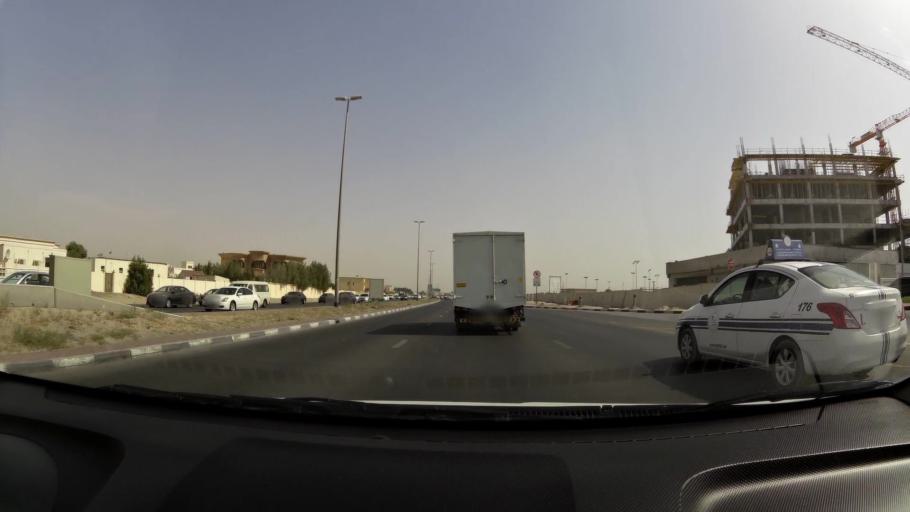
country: AE
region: Ash Shariqah
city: Sharjah
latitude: 25.2782
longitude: 55.3961
